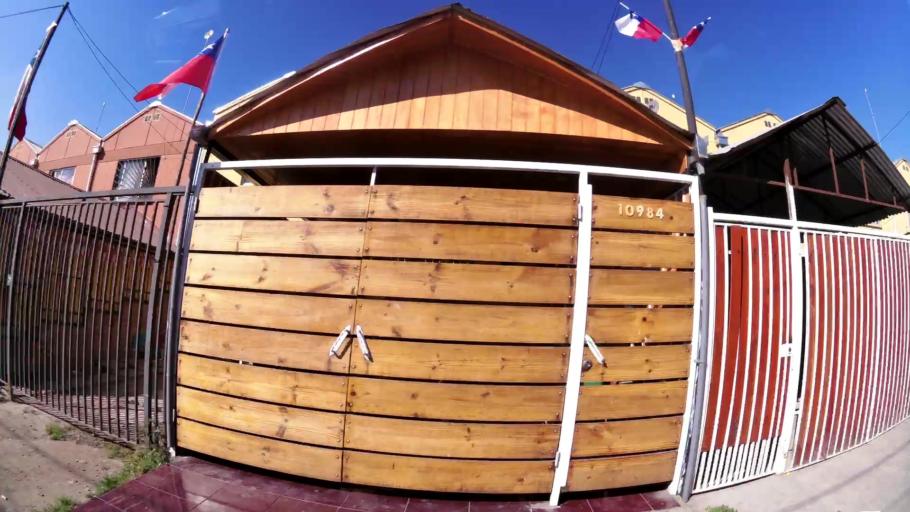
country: CL
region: Santiago Metropolitan
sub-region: Provincia de Santiago
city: La Pintana
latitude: -33.5628
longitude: -70.6187
